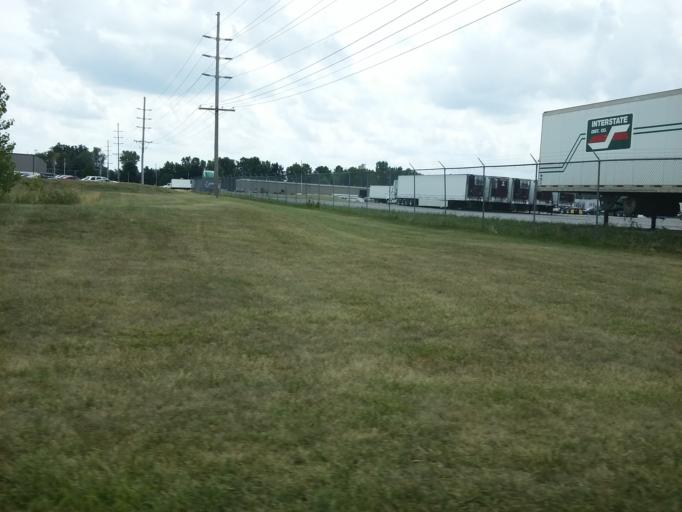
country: US
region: Ohio
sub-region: Hancock County
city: Findlay
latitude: 41.0549
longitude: -83.6794
